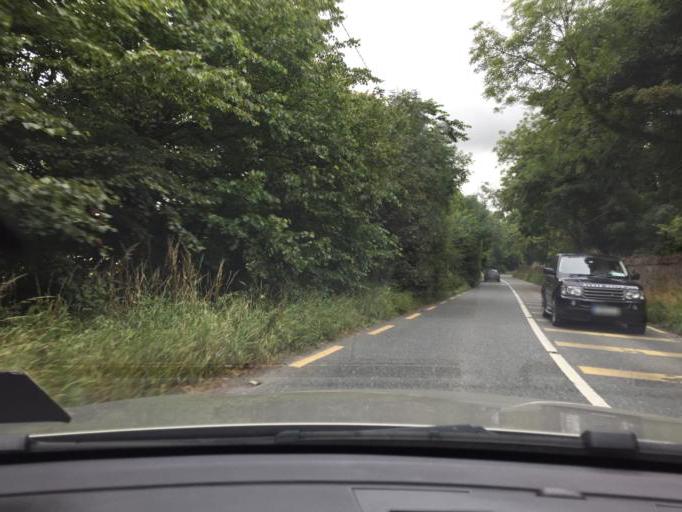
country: IE
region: Leinster
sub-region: Kildare
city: Maynooth
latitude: 53.3986
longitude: -6.5607
